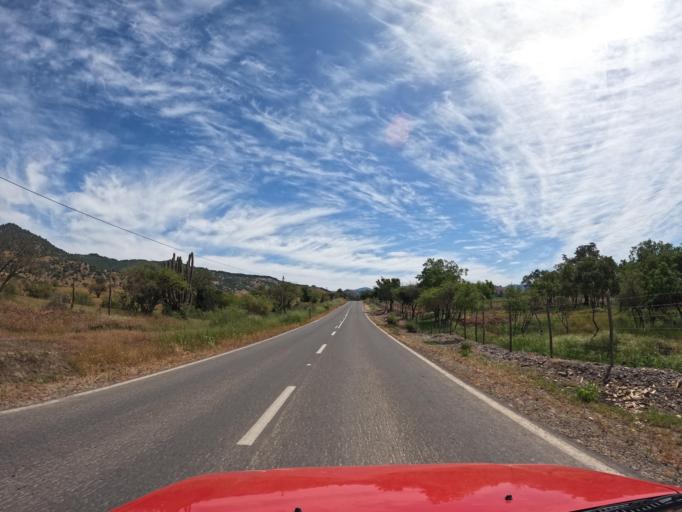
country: CL
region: Maule
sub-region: Provincia de Talca
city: Talca
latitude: -35.1220
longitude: -71.6668
